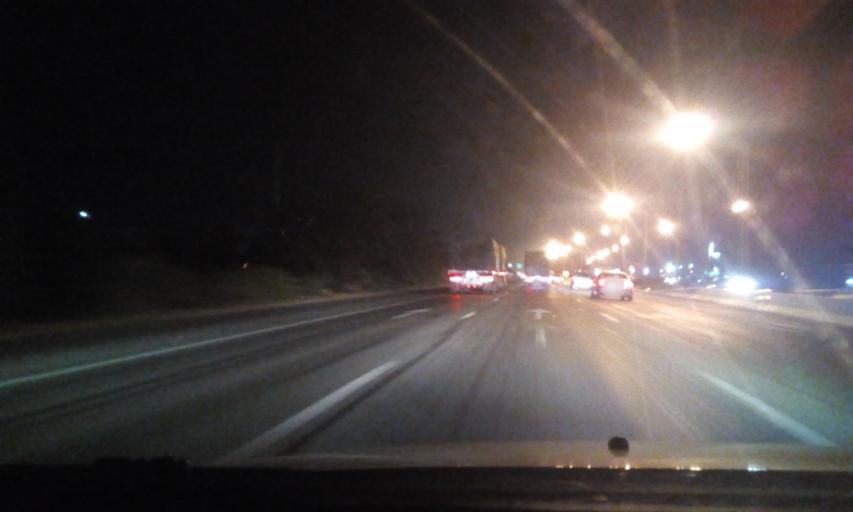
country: TH
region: Ang Thong
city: Chaiyo
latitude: 14.7291
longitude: 100.4553
